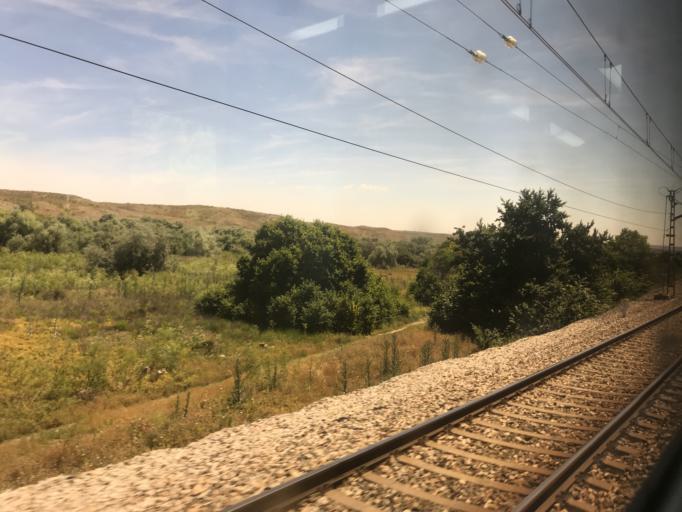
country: ES
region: Madrid
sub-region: Provincia de Madrid
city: Valdemoro
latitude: 40.1883
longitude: -3.6563
